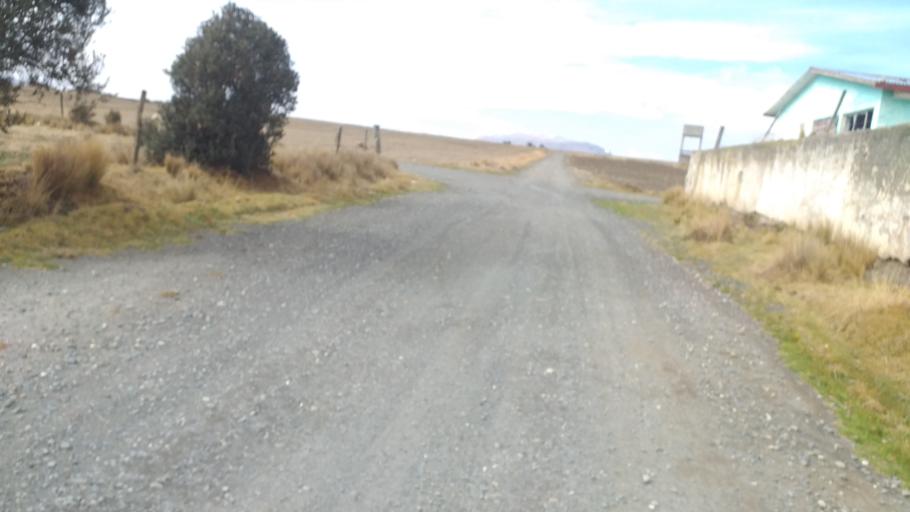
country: BO
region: La Paz
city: Achacachi
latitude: -16.0217
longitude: -68.7002
